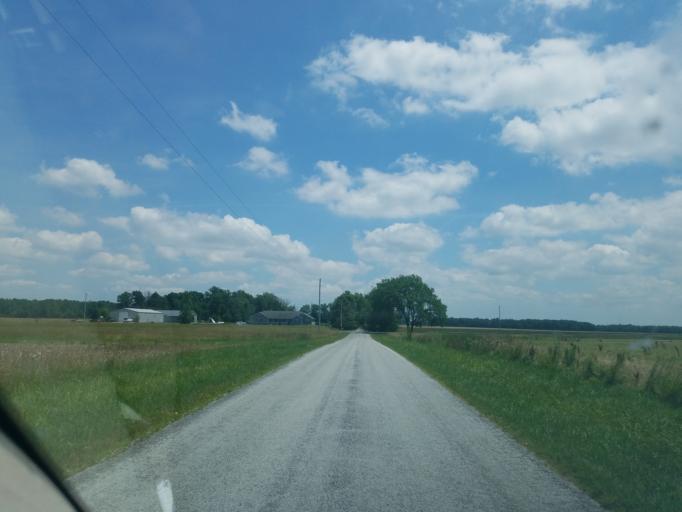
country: US
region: Ohio
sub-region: Hardin County
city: Forest
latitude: 40.7750
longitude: -83.6068
